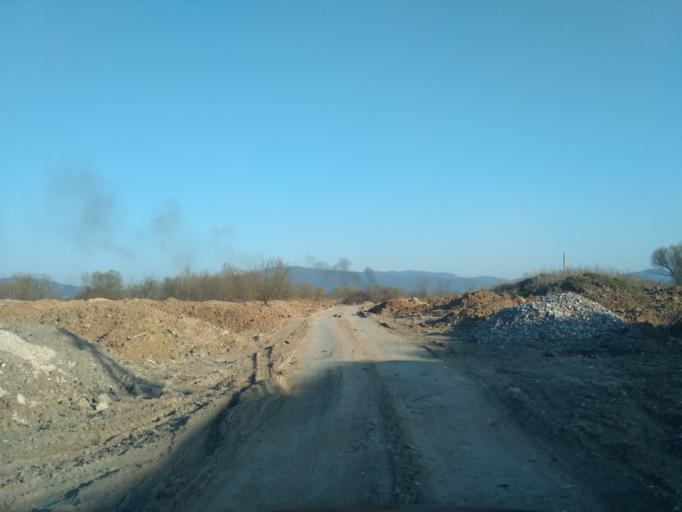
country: SK
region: Kosicky
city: Kosice
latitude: 48.6692
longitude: 21.3018
